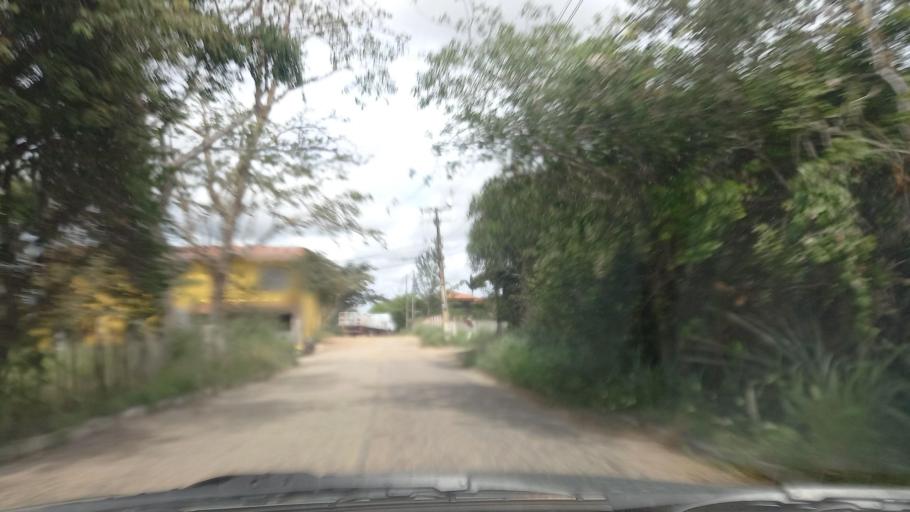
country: BR
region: Pernambuco
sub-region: Gravata
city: Gravata
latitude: -8.1846
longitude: -35.5803
